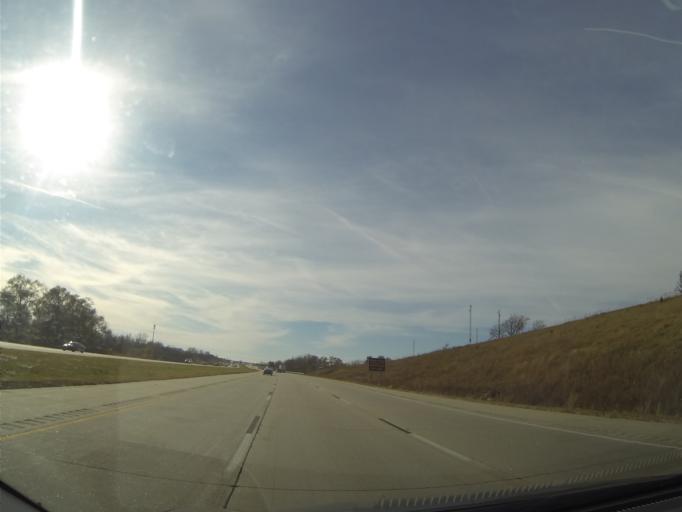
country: US
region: Nebraska
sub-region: Saunders County
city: Ashland
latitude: 41.0226
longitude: -96.3011
